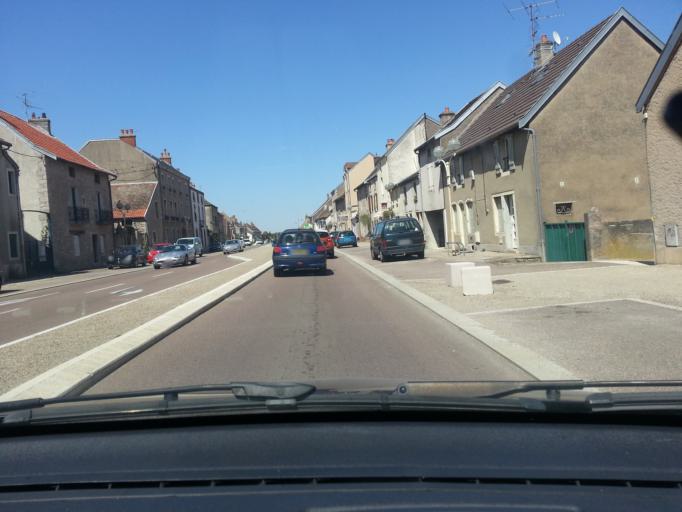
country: FR
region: Bourgogne
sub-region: Departement de la Cote-d'Or
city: Gevrey-Chambertin
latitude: 47.2275
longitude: 4.9798
